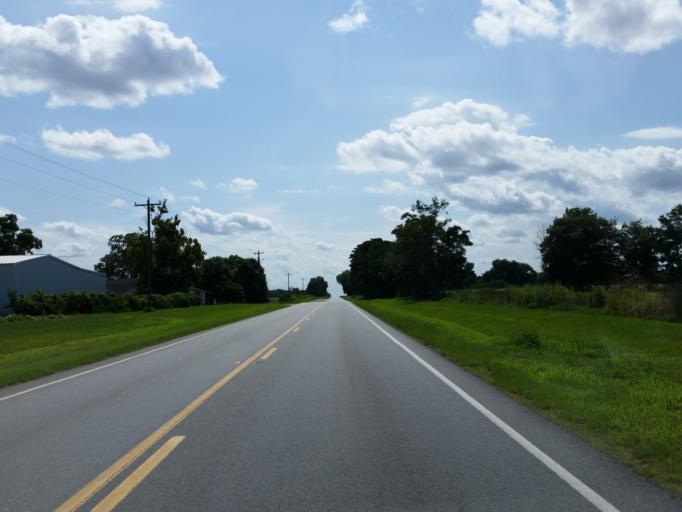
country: US
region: Georgia
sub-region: Turner County
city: Ashburn
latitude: 31.6359
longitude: -83.4796
